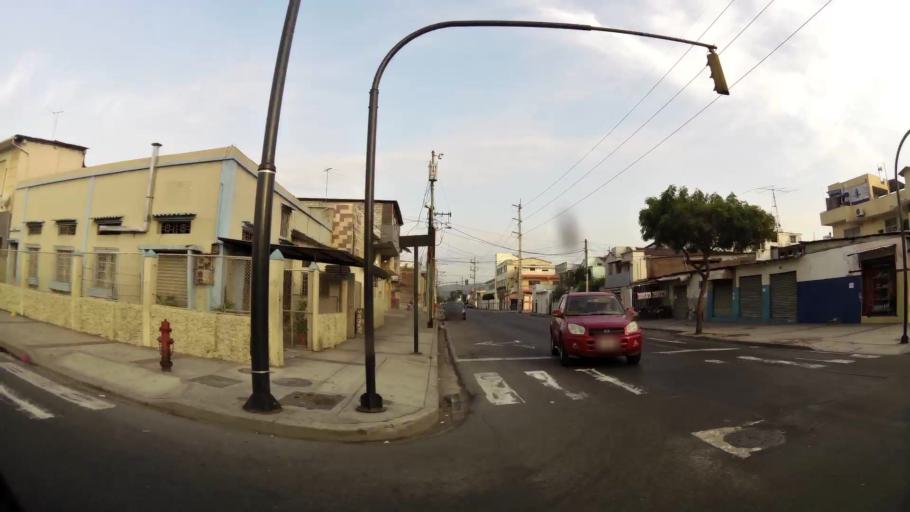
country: EC
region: Guayas
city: Guayaquil
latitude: -2.1918
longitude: -79.8954
